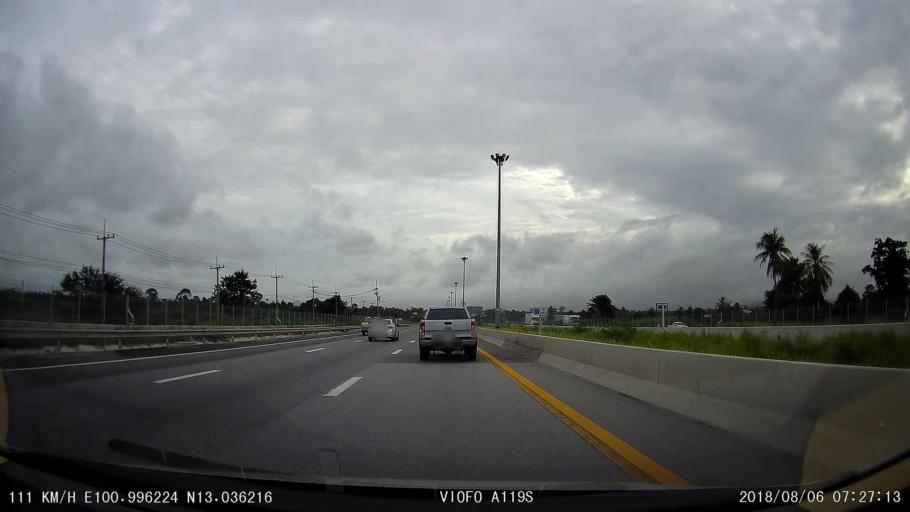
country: TH
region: Chon Buri
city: Ban Talat Bueng
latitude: 13.0364
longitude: 100.9959
